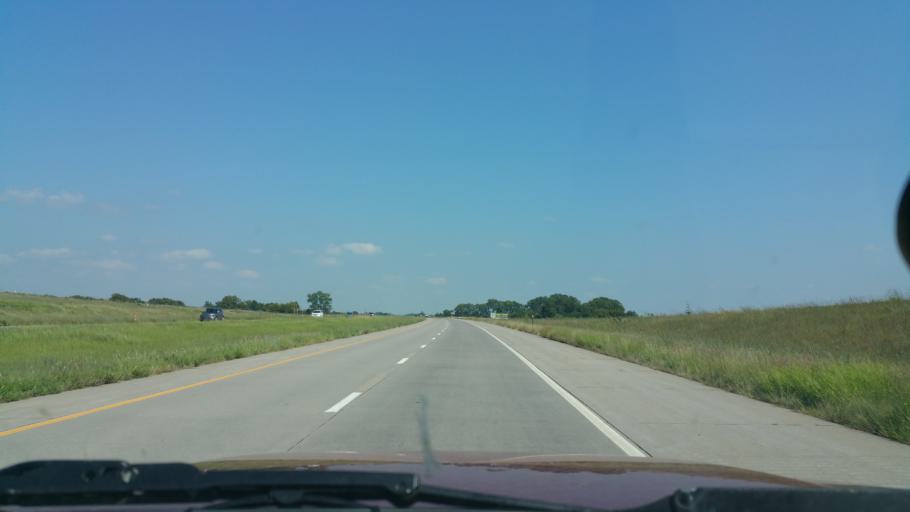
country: US
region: Kansas
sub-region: Dickinson County
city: Chapman
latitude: 38.9898
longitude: -96.9965
